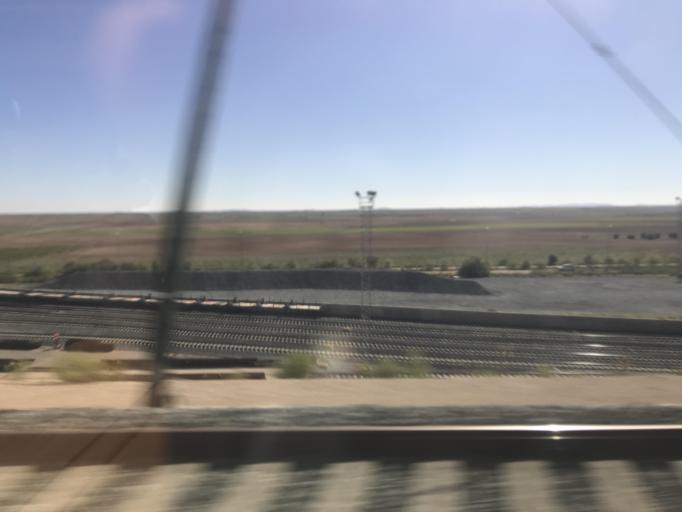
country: ES
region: Castille-La Mancha
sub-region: Province of Toledo
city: Villarrubia de Santiago
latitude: 39.9597
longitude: -3.3498
